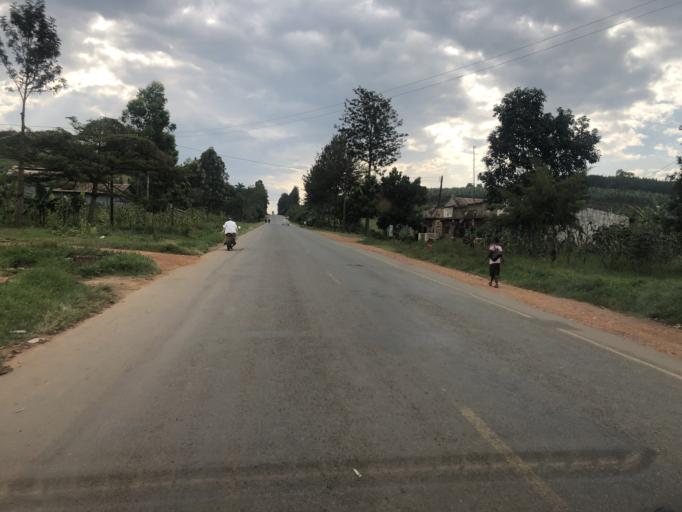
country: UG
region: Western Region
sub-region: Sheema District
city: Kibingo
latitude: -0.5633
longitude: 30.3409
